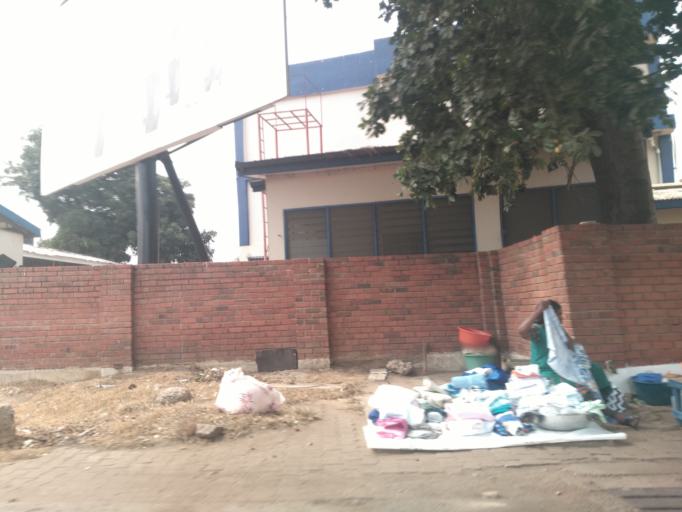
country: GH
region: Greater Accra
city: Accra
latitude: 5.5678
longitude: -0.1808
